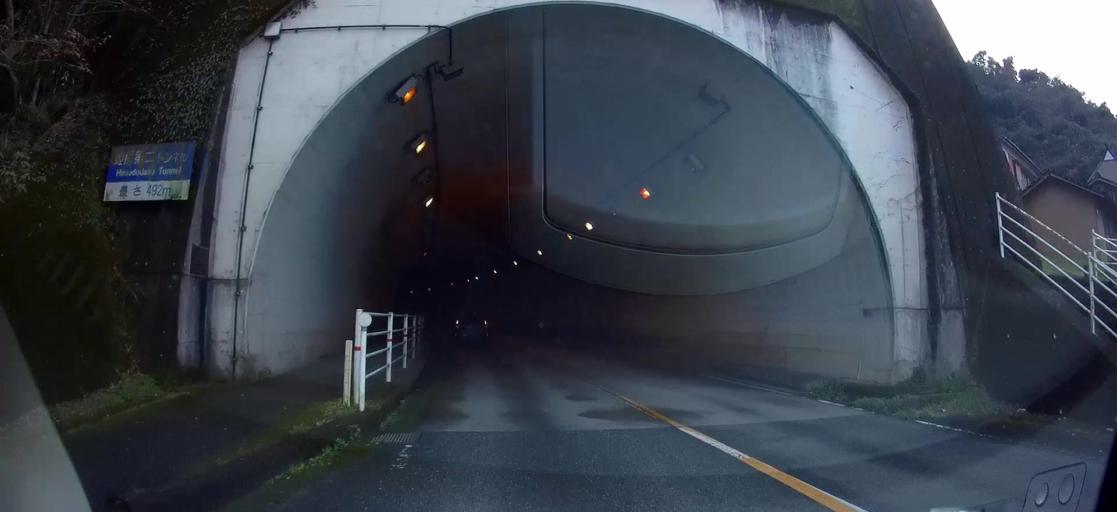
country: JP
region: Kumamoto
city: Yatsushiro
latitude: 32.4407
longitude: 130.4055
